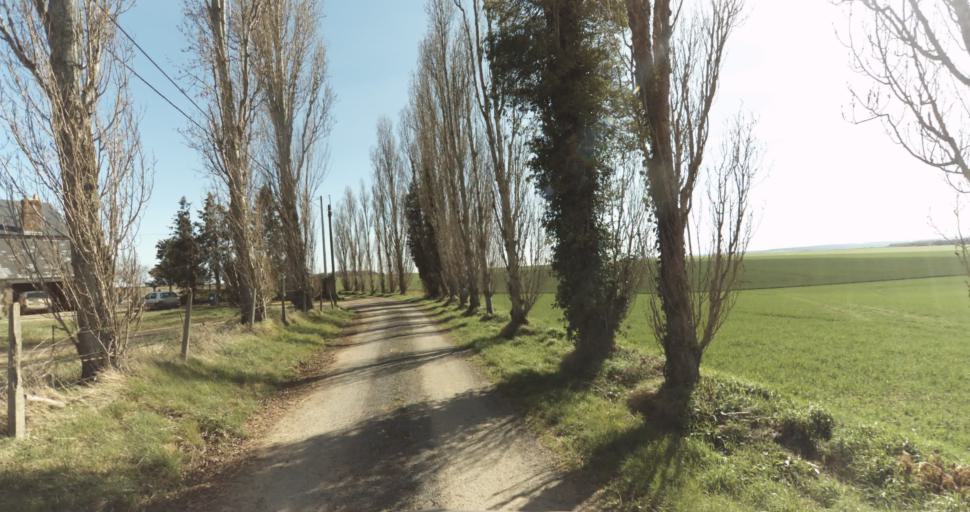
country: FR
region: Lower Normandy
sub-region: Departement du Calvados
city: Saint-Pierre-sur-Dives
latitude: 49.0025
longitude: -0.0439
